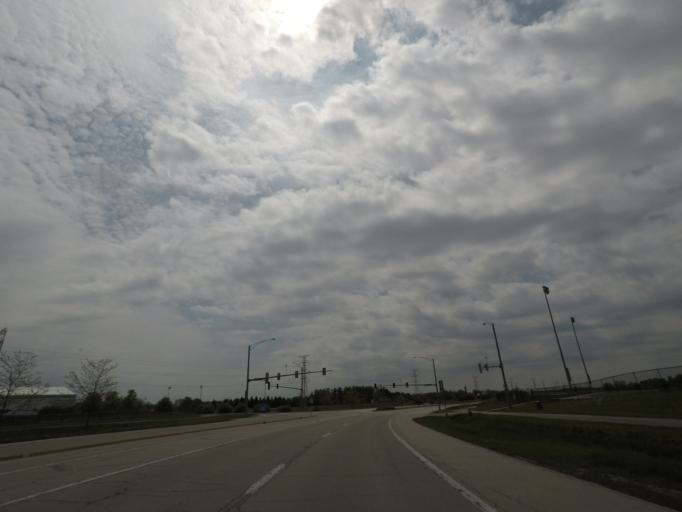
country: US
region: Illinois
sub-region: Winnebago County
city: Cherry Valley
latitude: 42.3226
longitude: -88.9487
